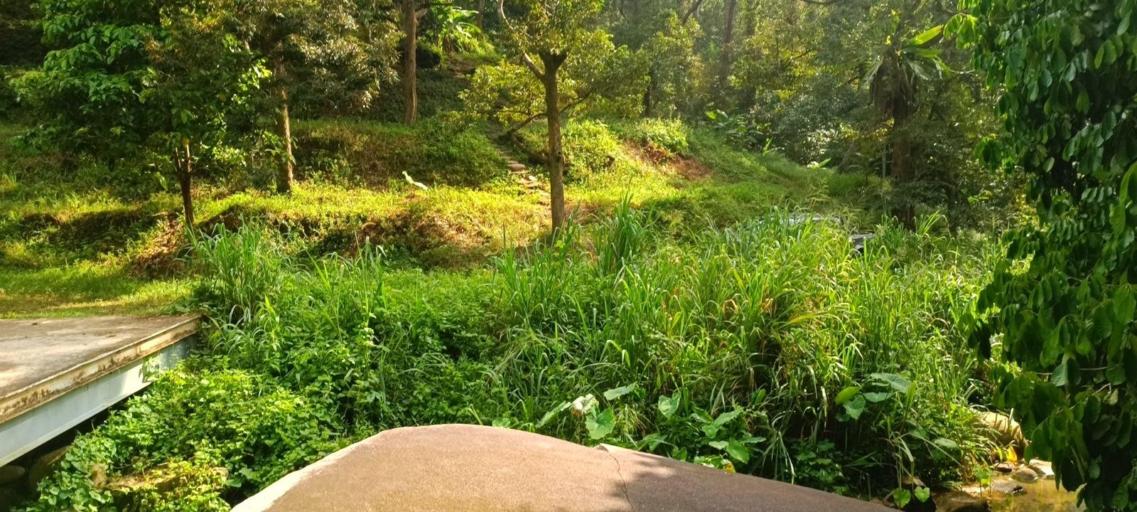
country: MY
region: Penang
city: Kampung Sungai Ara
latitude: 5.3235
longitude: 100.2517
